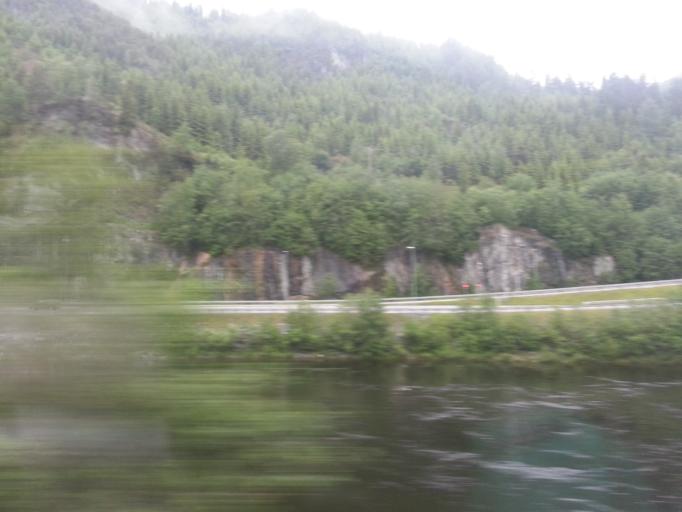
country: NO
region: Sor-Trondelag
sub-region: Midtre Gauldal
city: Storen
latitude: 63.0674
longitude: 10.2838
